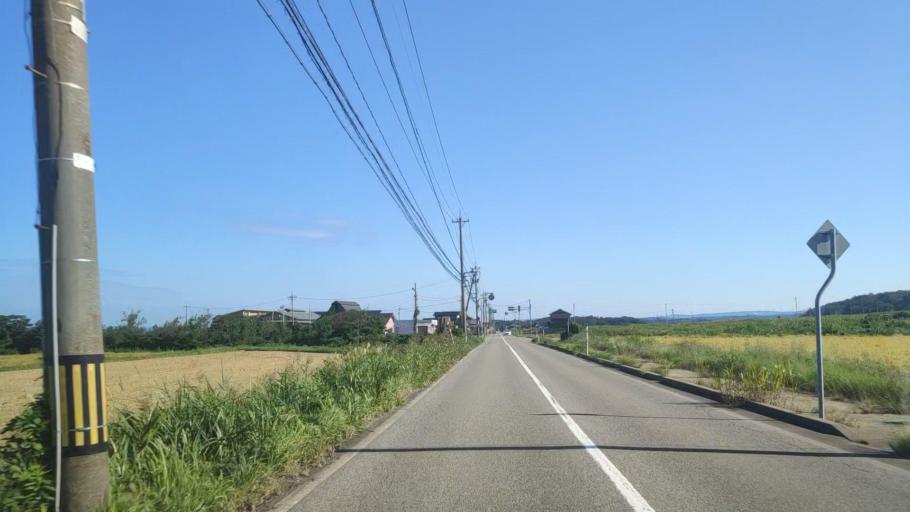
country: JP
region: Ishikawa
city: Hakui
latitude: 36.9378
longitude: 136.7594
